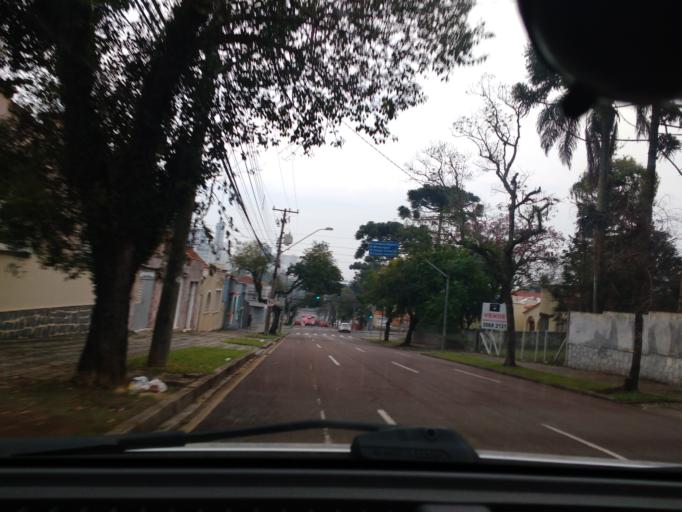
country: BR
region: Parana
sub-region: Curitiba
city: Curitiba
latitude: -25.4250
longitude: -49.2826
